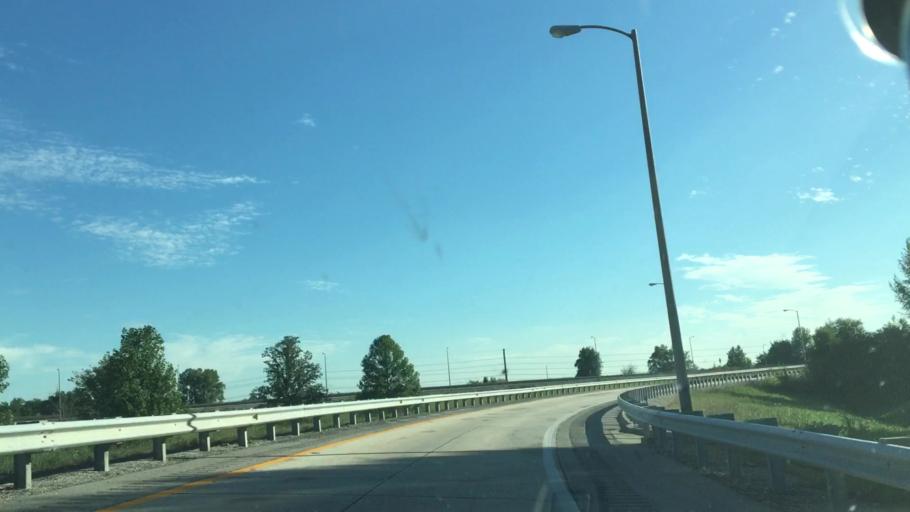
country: US
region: Kentucky
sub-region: Daviess County
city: Owensboro
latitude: 37.7672
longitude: -87.1647
